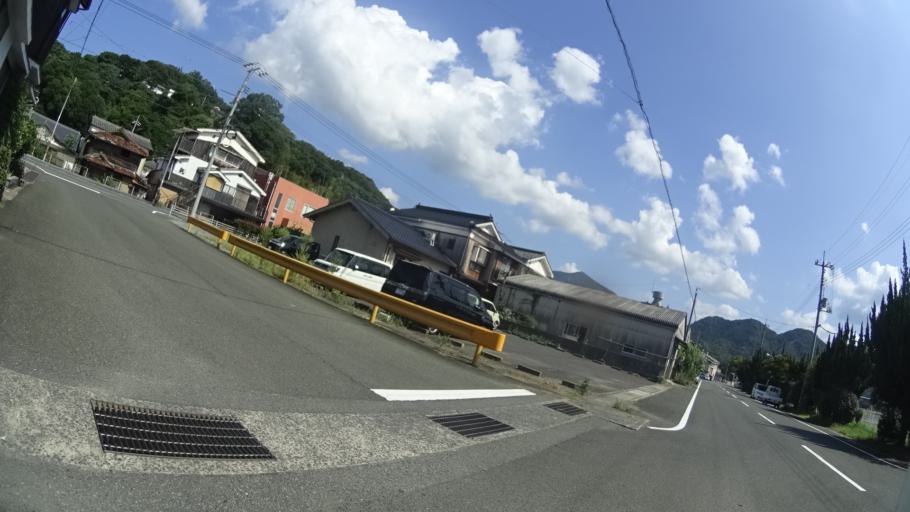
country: JP
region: Yamaguchi
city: Hagi
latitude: 34.4313
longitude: 131.4150
